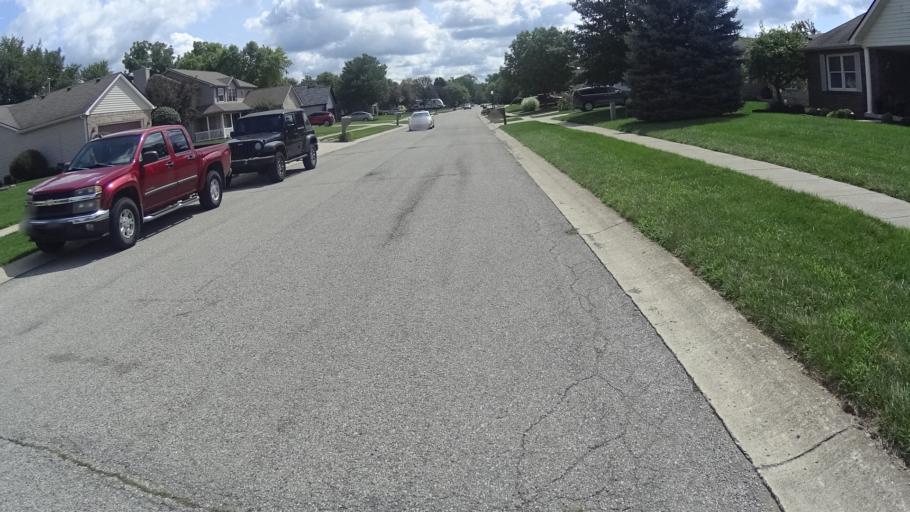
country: US
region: Indiana
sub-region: Madison County
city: Pendleton
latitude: 40.0136
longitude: -85.7463
